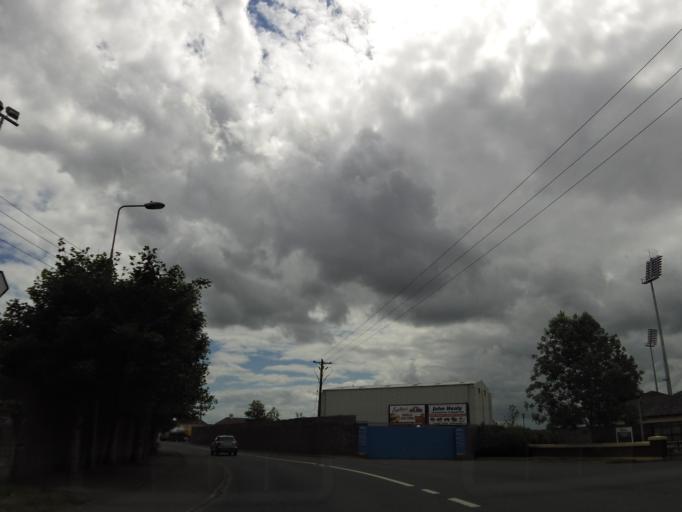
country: IE
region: Munster
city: Thurles
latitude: 52.6839
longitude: -7.8242
